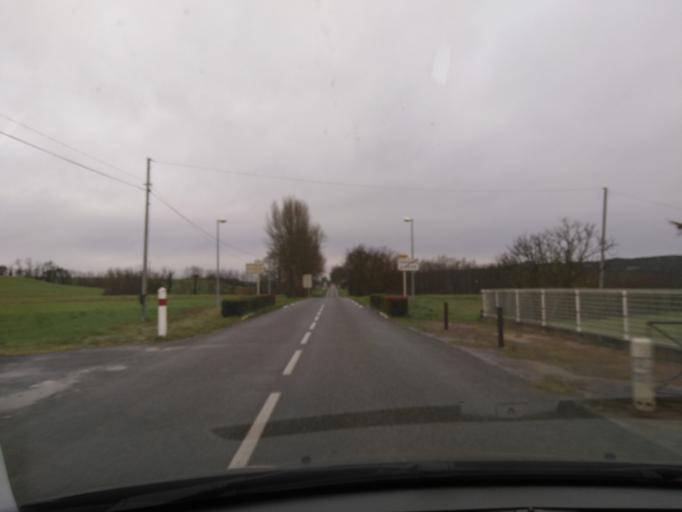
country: FR
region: Midi-Pyrenees
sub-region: Departement de la Haute-Garonne
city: Montesquieu-Volvestre
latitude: 43.1858
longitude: 1.2402
